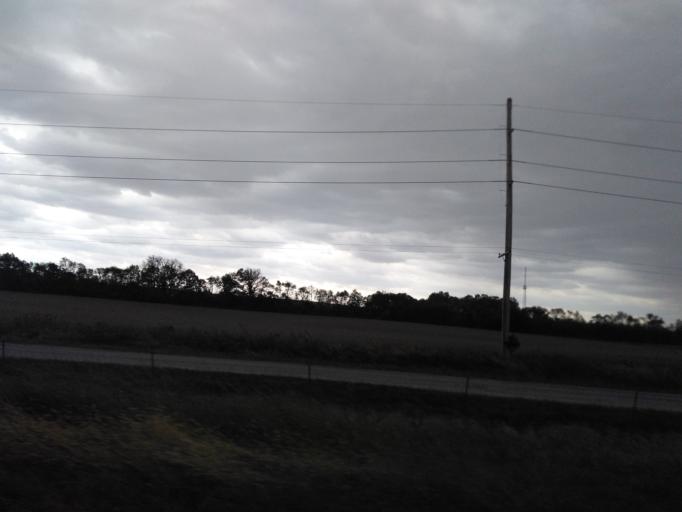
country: US
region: Illinois
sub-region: Bond County
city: Greenville
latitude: 38.8505
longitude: -89.4611
